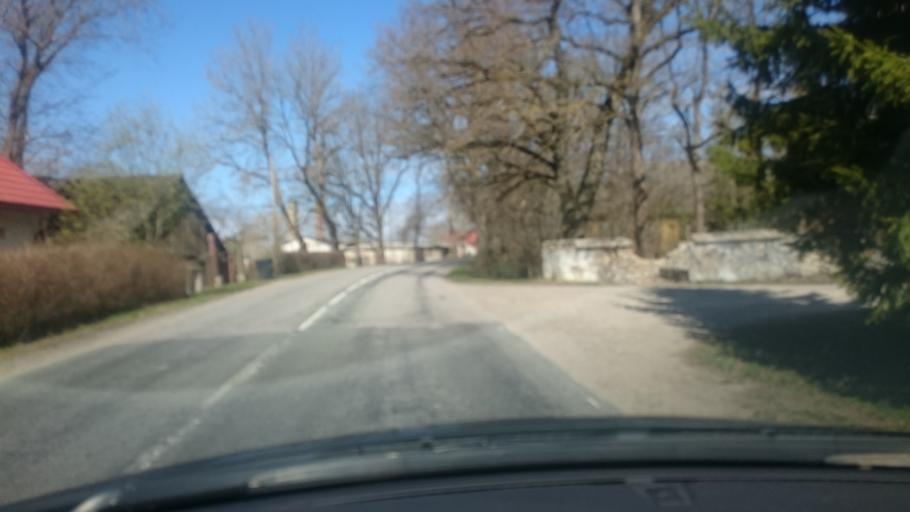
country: EE
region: Harju
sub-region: Raasiku vald
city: Raasiku
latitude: 59.1034
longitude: 25.1682
